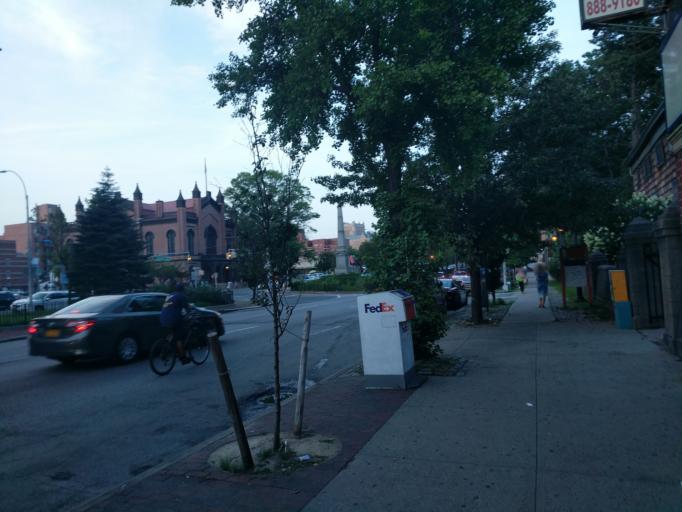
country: US
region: New York
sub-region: Queens County
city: Jamaica
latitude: 40.7630
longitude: -73.8308
